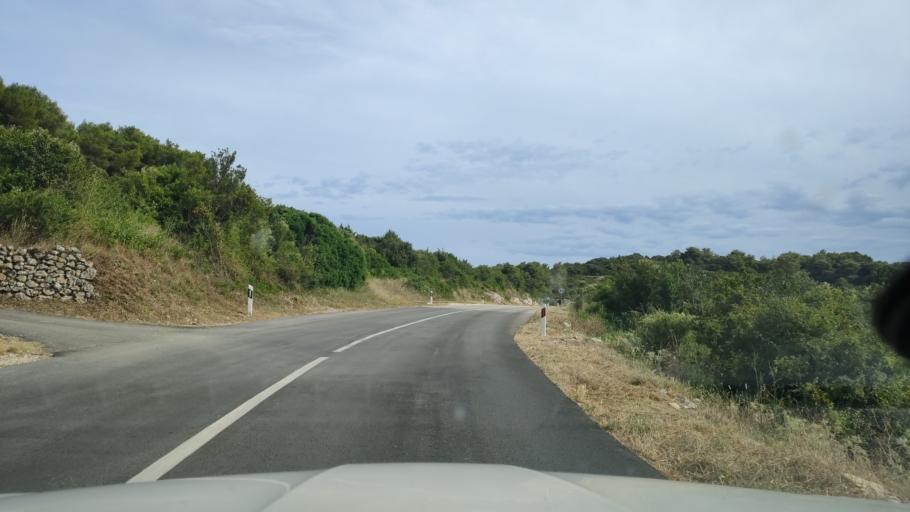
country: HR
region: Splitsko-Dalmatinska
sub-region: Grad Vis
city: Vis
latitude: 43.0392
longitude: 16.2006
